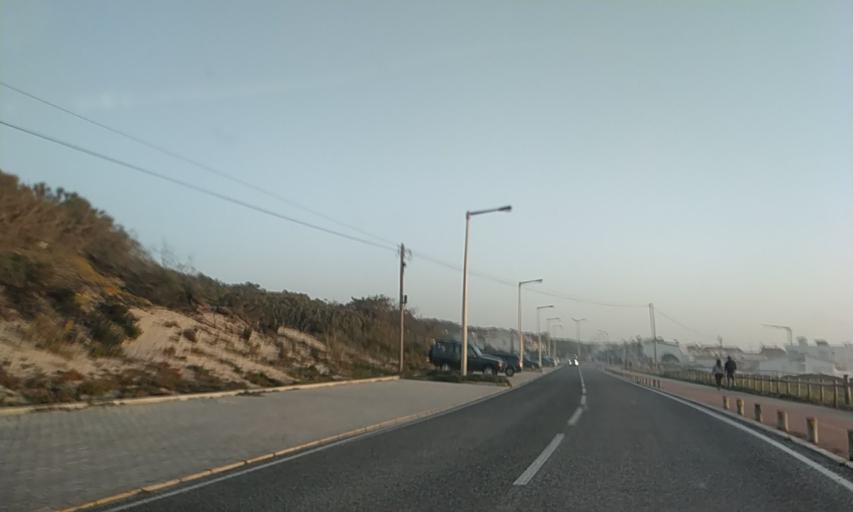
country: PT
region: Leiria
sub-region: Alcobaca
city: Pataias
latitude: 39.7630
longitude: -9.0310
